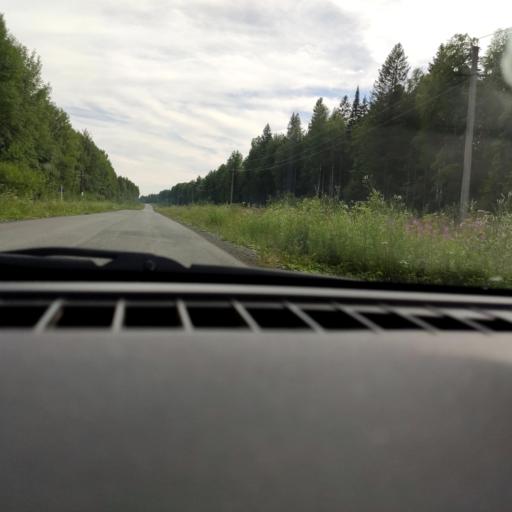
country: RU
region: Perm
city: Polazna
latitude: 58.3272
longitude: 56.1503
